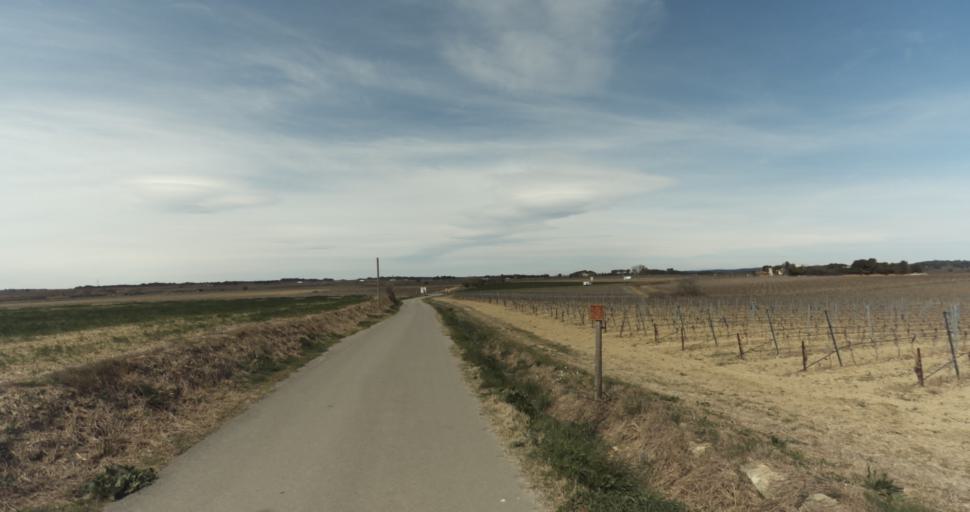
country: FR
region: Languedoc-Roussillon
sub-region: Departement de l'Herault
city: Pinet
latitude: 43.4101
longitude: 3.5451
